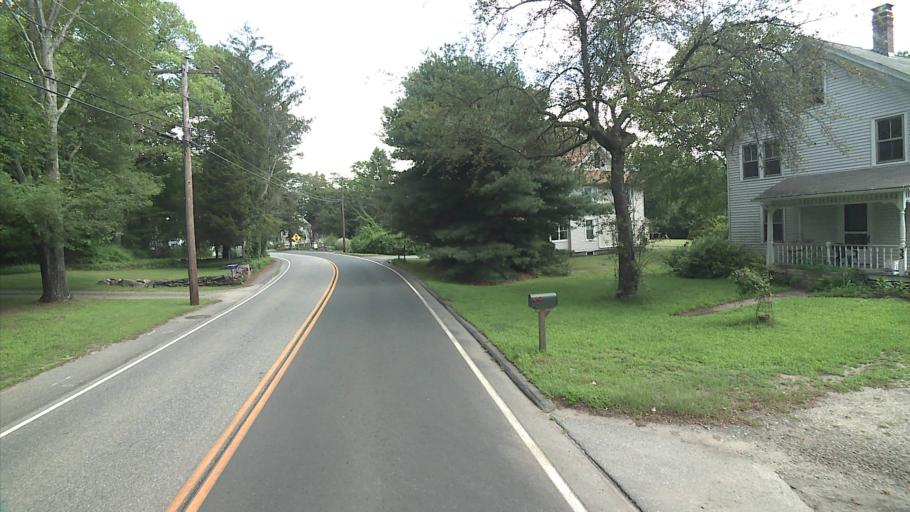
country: US
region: Connecticut
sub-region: Middlesex County
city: Essex Village
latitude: 41.3495
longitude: -72.4164
